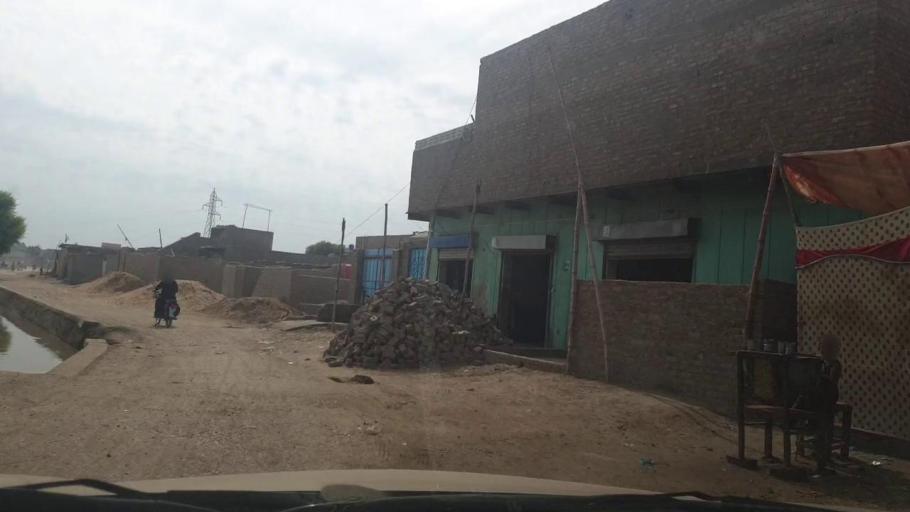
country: PK
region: Sindh
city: Larkana
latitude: 27.5812
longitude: 68.2052
